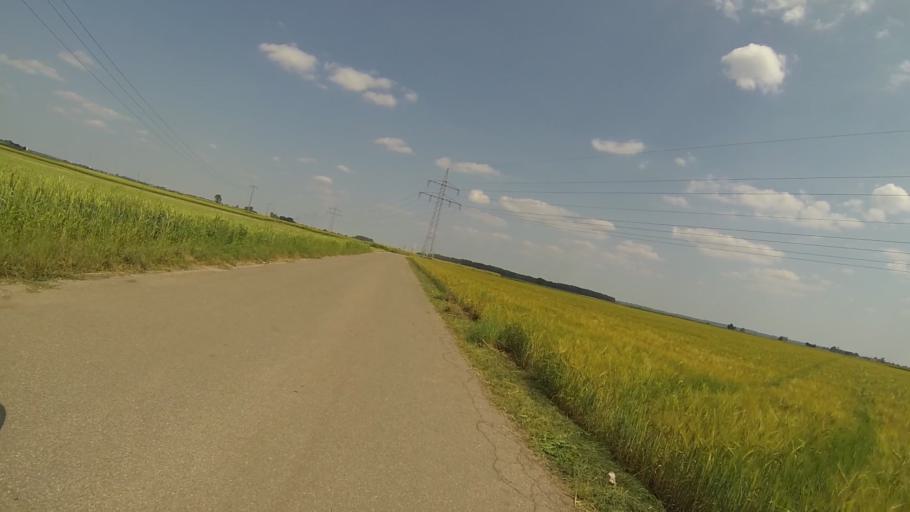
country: DE
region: Baden-Wuerttemberg
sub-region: Regierungsbezirk Stuttgart
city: Niederstotzingen
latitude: 48.5310
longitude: 10.2491
